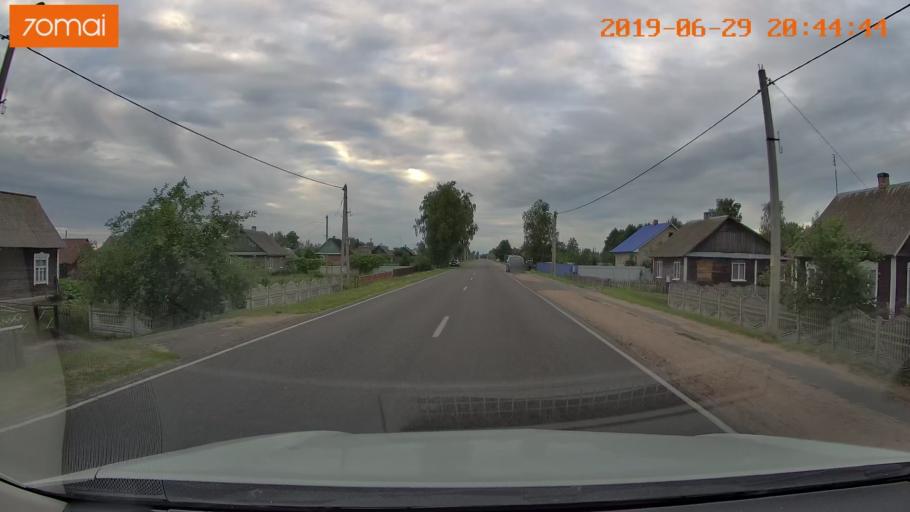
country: BY
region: Brest
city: Hantsavichy
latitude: 52.6166
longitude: 26.3074
